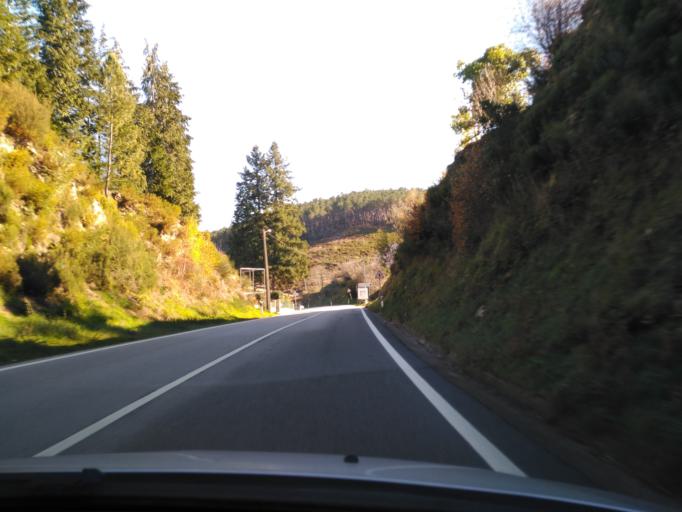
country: PT
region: Braga
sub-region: Cabeceiras de Basto
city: Cabeceiras de Basto
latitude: 41.6729
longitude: -7.9756
